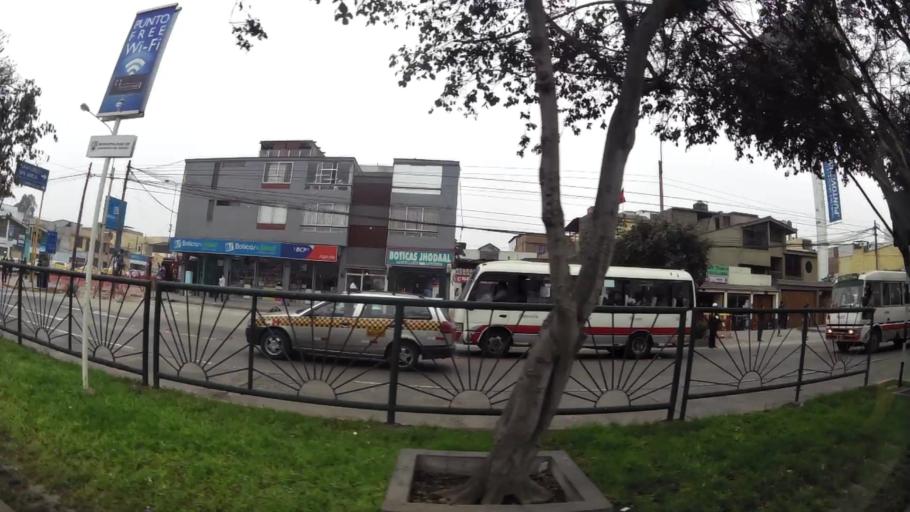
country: PE
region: Lima
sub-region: Lima
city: Surco
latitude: -12.1299
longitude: -76.9815
